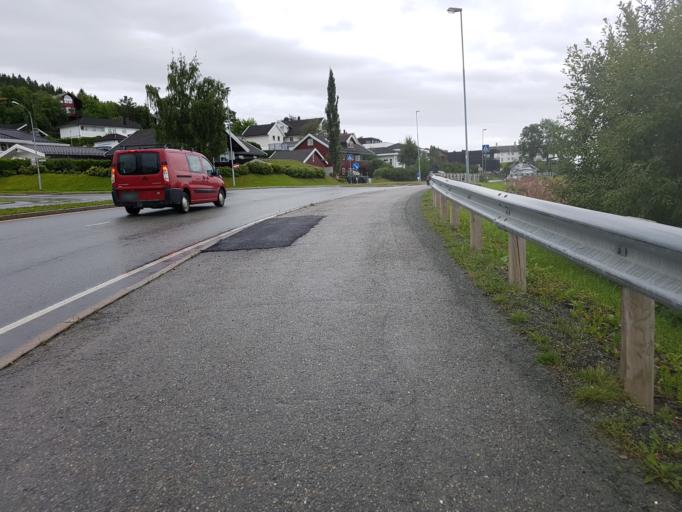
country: NO
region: Sor-Trondelag
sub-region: Trondheim
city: Trondheim
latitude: 63.4019
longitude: 10.4466
